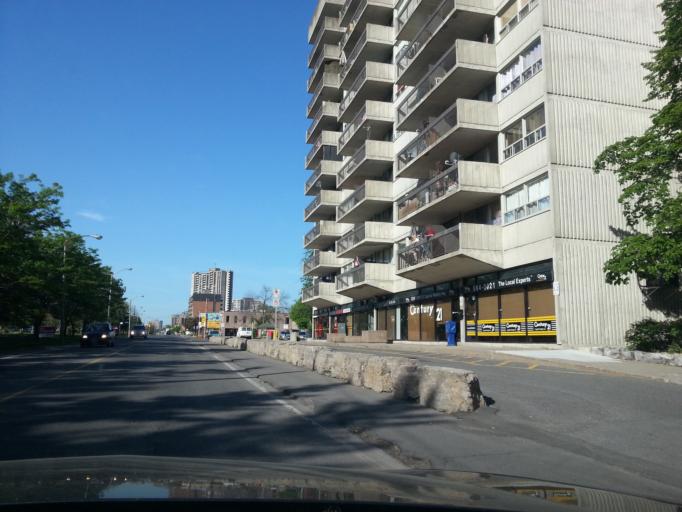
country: CA
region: Ontario
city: Ottawa
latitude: 45.3801
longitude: -75.7724
